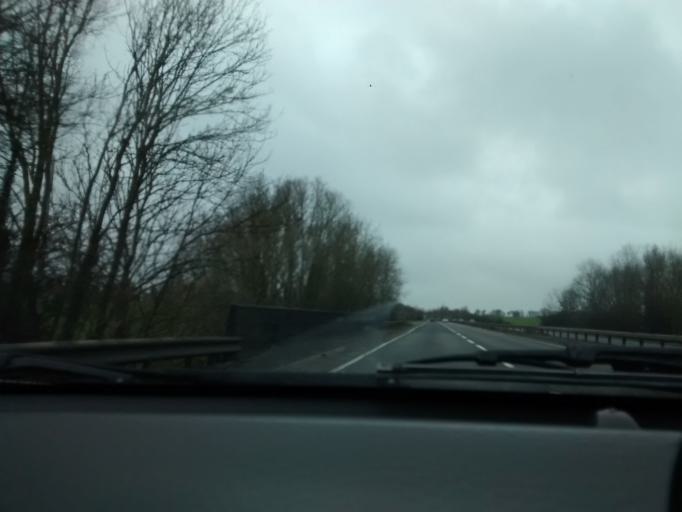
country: GB
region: England
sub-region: Suffolk
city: Needham Market
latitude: 52.1704
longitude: 1.0536
